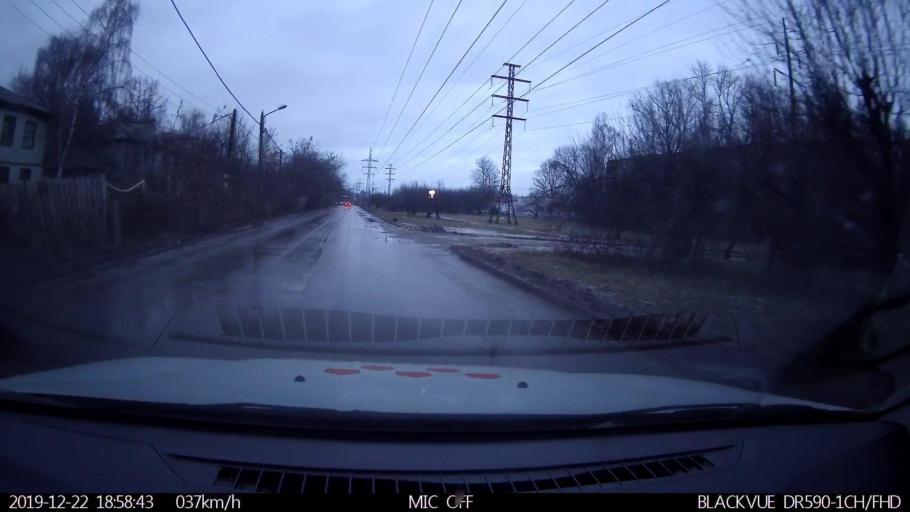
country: RU
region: Nizjnij Novgorod
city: Gorbatovka
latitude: 56.3440
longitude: 43.8443
